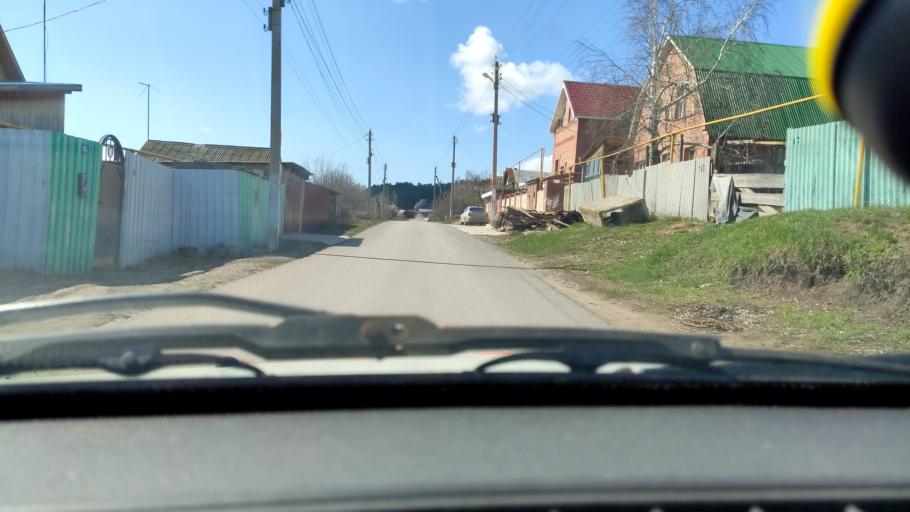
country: RU
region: Samara
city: Zhigulevsk
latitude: 53.5427
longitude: 49.5225
